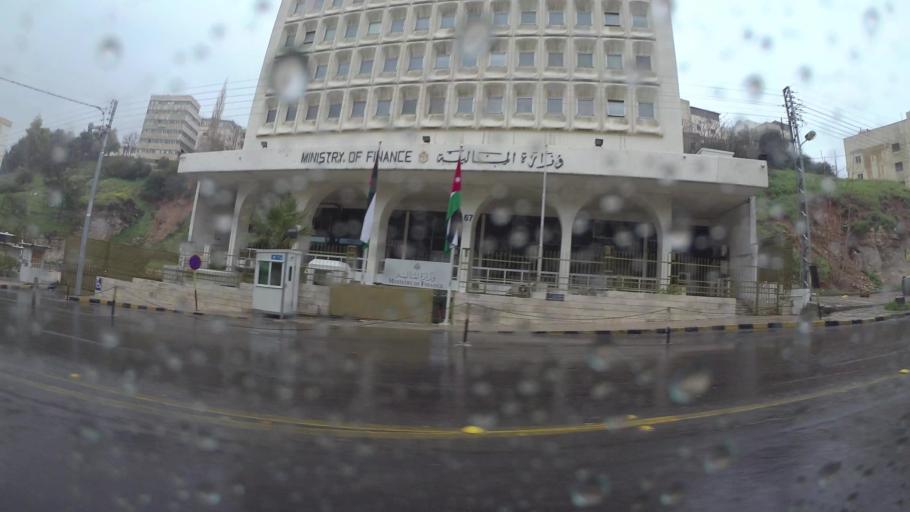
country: JO
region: Amman
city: Amman
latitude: 31.9584
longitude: 35.9290
